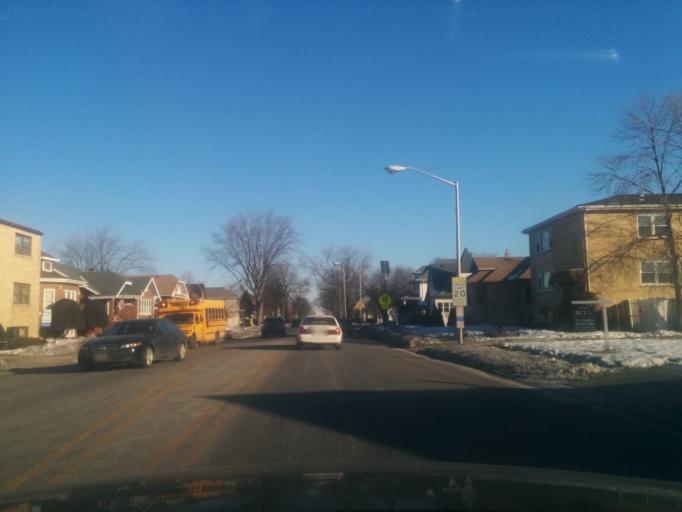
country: US
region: Illinois
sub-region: Cook County
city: Franklin Park
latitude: 41.9302
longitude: -87.8652
